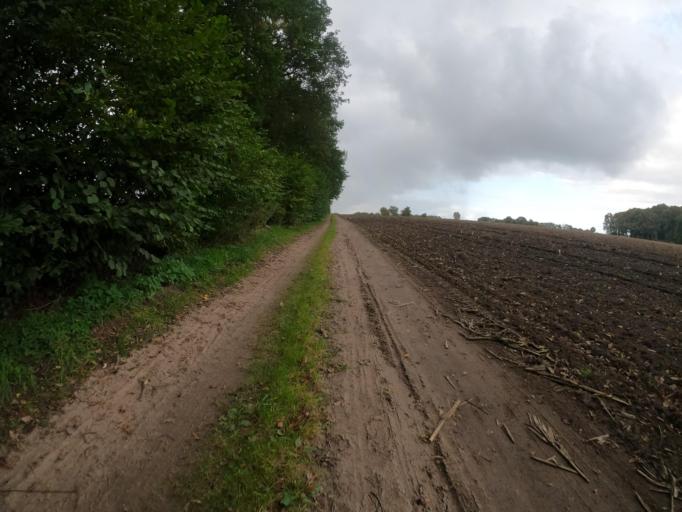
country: DE
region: North Rhine-Westphalia
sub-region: Regierungsbezirk Dusseldorf
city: Schermbeck
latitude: 51.7234
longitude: 6.8747
